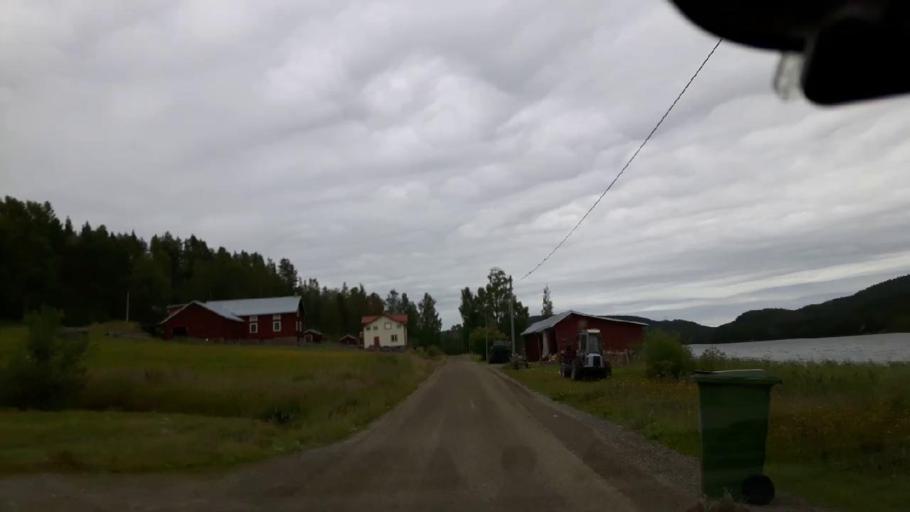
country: SE
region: Jaemtland
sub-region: Braecke Kommun
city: Braecke
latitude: 63.0015
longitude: 15.3811
